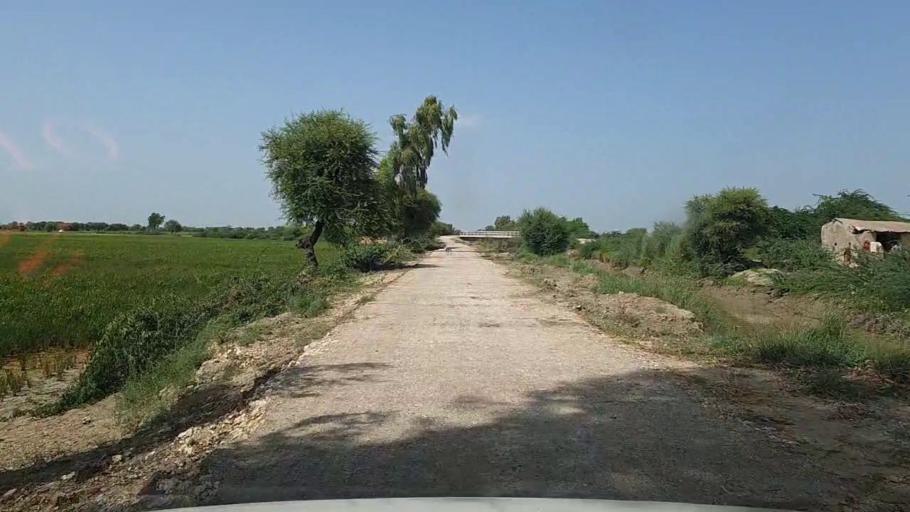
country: PK
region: Sindh
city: Kario
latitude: 24.6609
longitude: 68.5483
